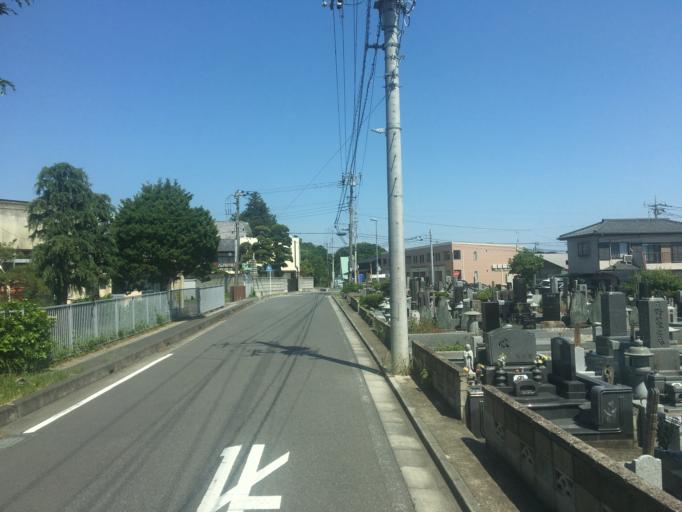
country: JP
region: Saitama
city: Ogawa
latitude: 36.0397
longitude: 139.3242
